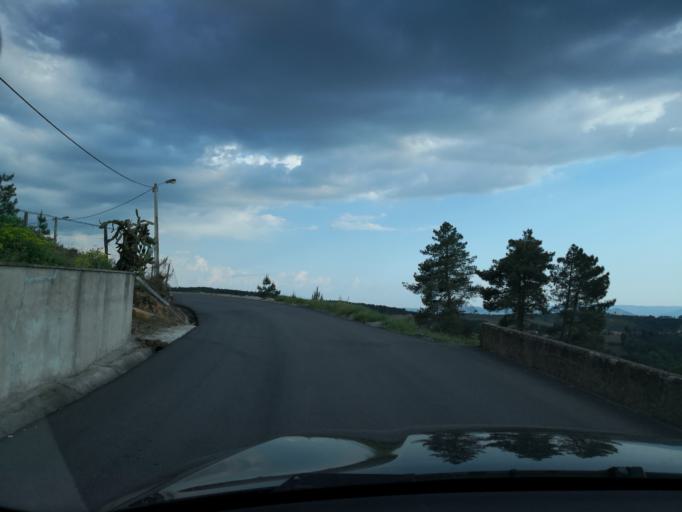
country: PT
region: Vila Real
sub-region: Sabrosa
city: Vilela
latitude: 41.2228
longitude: -7.6820
